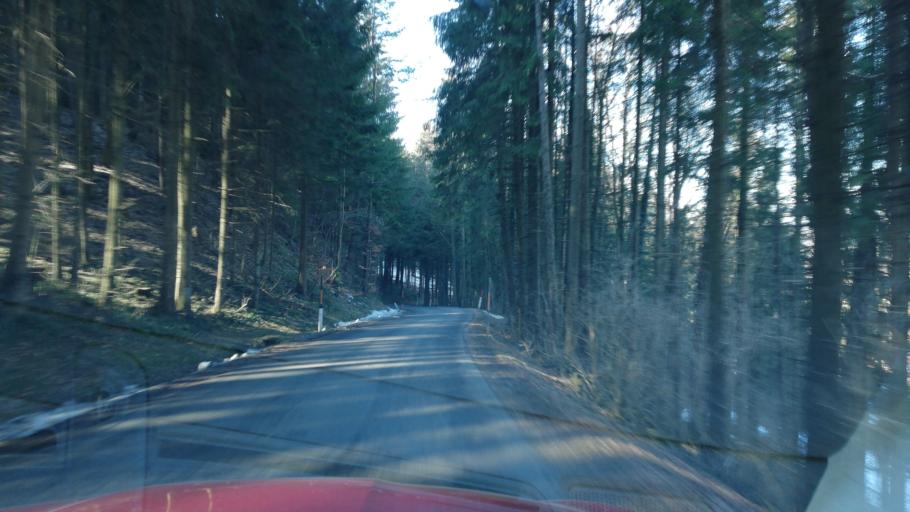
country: AT
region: Upper Austria
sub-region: Politischer Bezirk Vocklabruck
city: Vocklabruck
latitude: 47.9854
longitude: 13.6567
